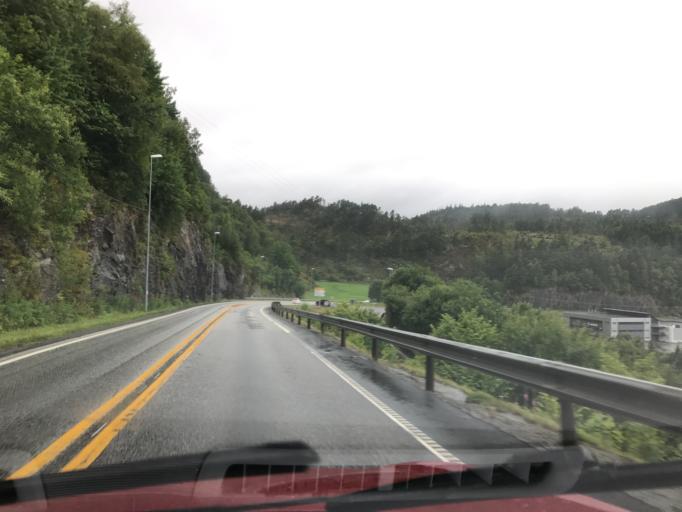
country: NO
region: Vest-Agder
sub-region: Flekkefjord
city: Flekkefjord
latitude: 58.2811
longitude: 6.7107
